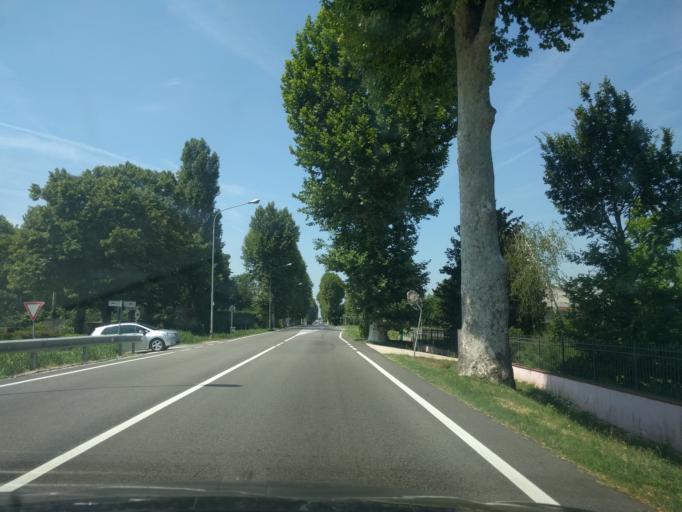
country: IT
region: Veneto
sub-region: Provincia di Padova
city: Boara Pisani
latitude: 45.1098
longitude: 11.7796
